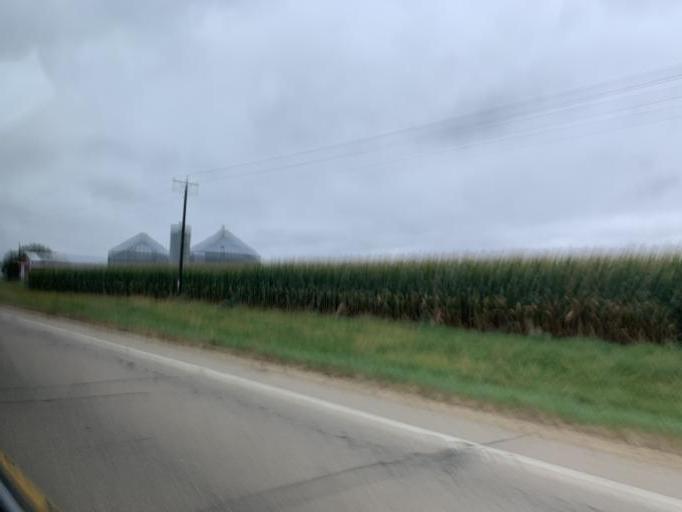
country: US
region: Wisconsin
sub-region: Grant County
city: Muscoda
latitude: 43.2198
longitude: -90.5069
